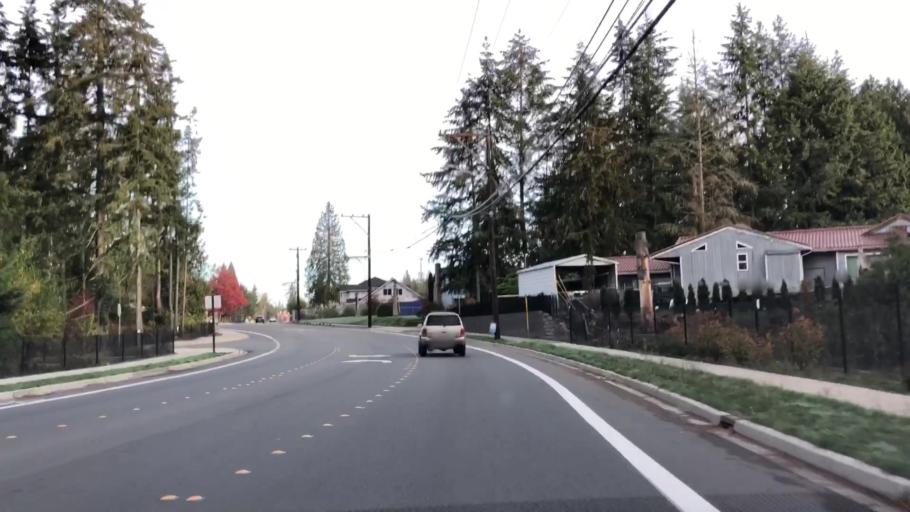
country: US
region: Washington
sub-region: Snohomish County
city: Martha Lake
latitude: 47.8431
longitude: -122.2357
